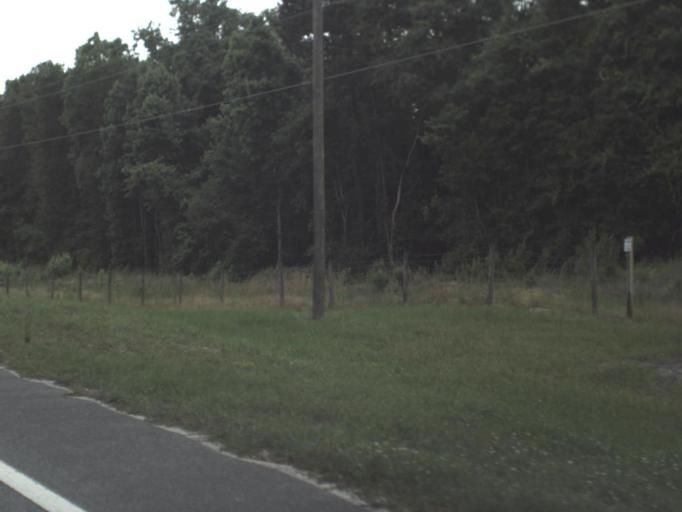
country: US
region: Florida
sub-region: Clay County
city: Asbury Lake
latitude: 29.9105
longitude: -81.8974
